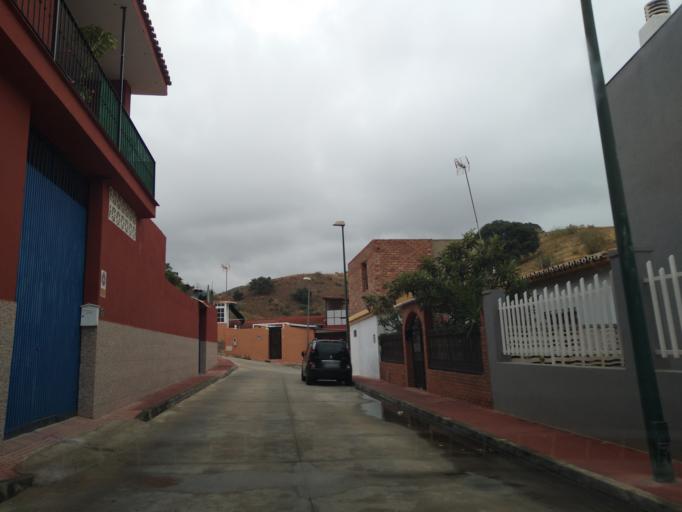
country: ES
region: Andalusia
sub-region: Provincia de Malaga
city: Malaga
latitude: 36.7484
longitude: -4.4779
